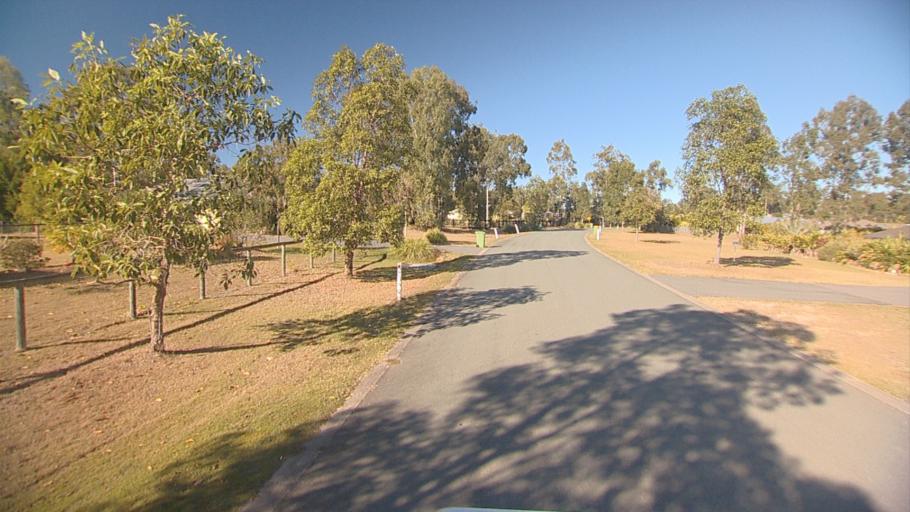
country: AU
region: Queensland
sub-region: Logan
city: North Maclean
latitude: -27.7561
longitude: 152.9672
